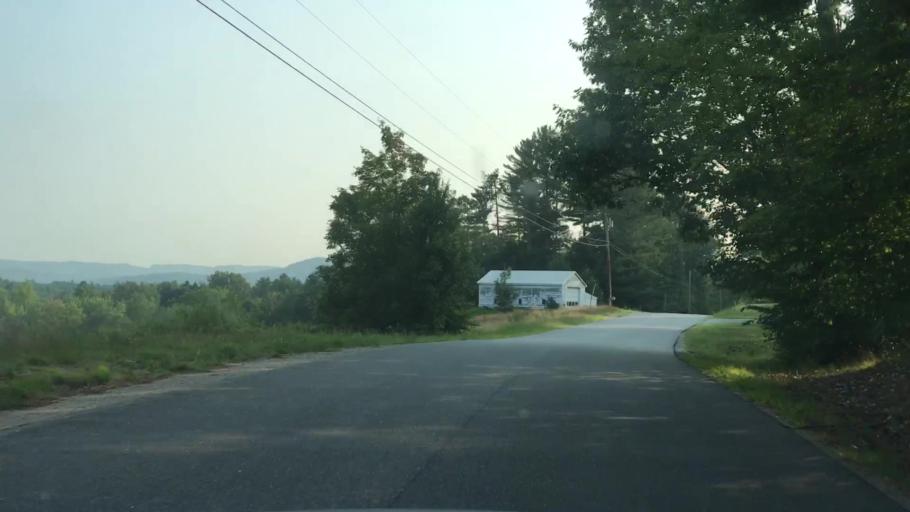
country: US
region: Maine
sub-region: Oxford County
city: Bethel
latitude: 44.4165
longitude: -70.8561
